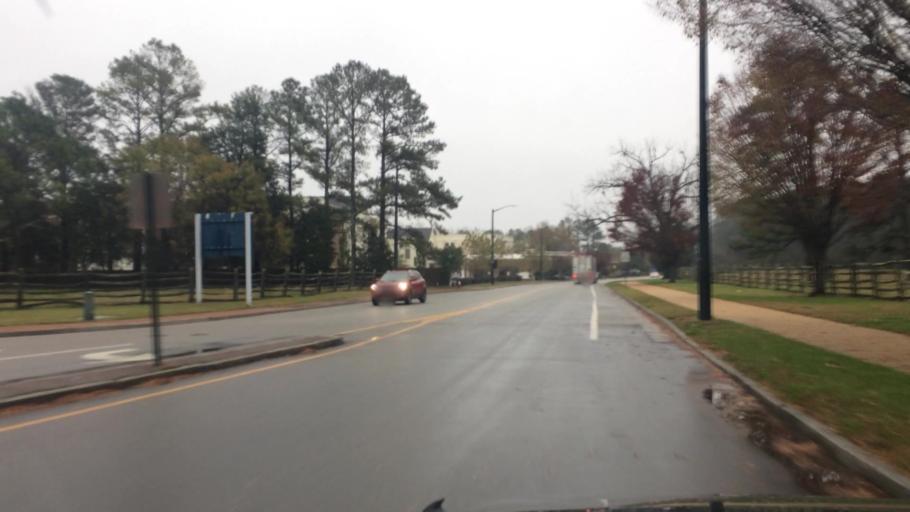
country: US
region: Virginia
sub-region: City of Williamsburg
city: Williamsburg
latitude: 37.2708
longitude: -76.6889
